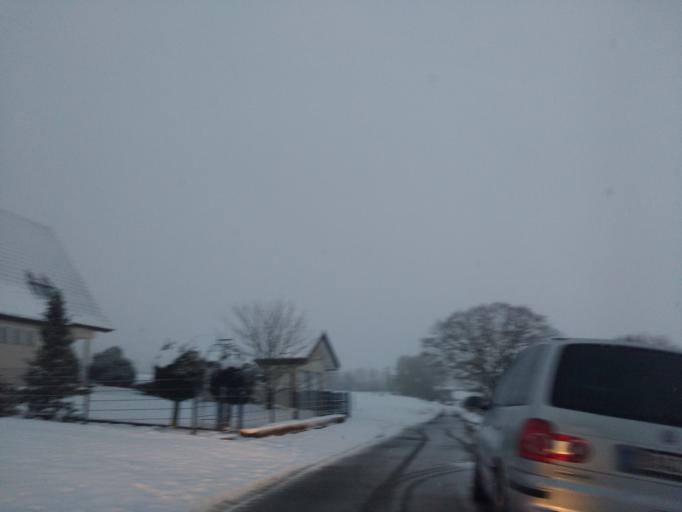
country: DE
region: North Rhine-Westphalia
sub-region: Regierungsbezirk Detmold
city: Horn
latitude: 51.8218
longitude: 8.9415
